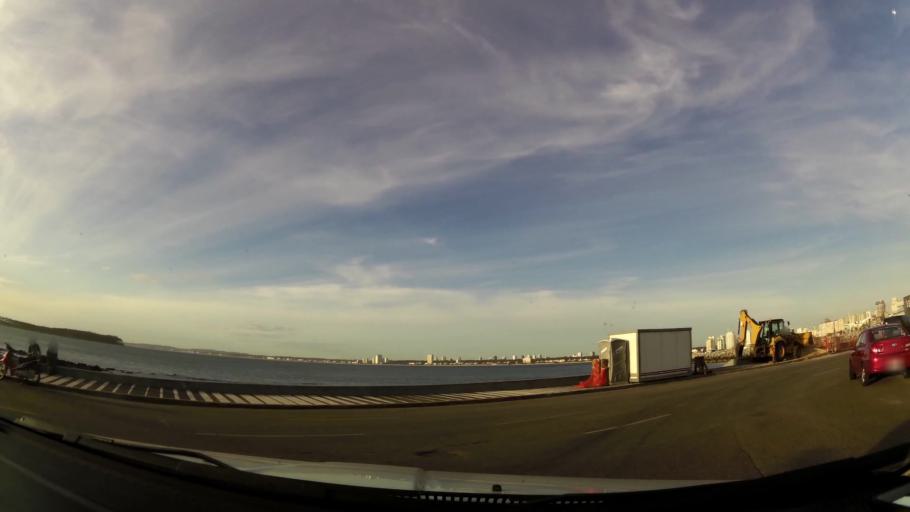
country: UY
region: Maldonado
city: Punta del Este
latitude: -34.9647
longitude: -54.9536
